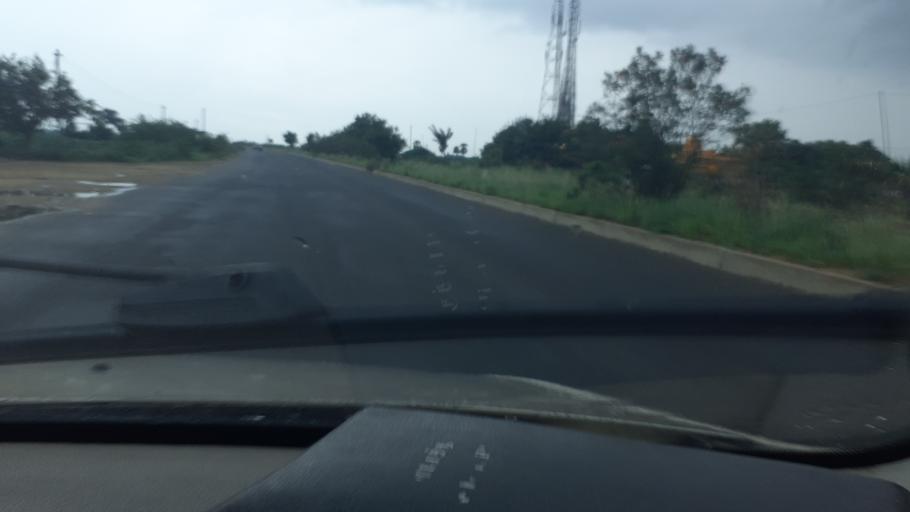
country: IN
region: Tamil Nadu
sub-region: Thoothukkudi
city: Kadambur
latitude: 9.0661
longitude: 77.7986
